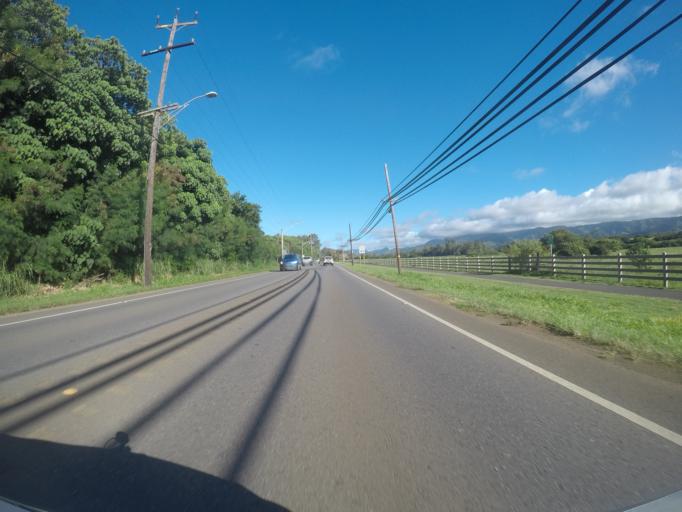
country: US
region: Hawaii
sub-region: Honolulu County
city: La'ie
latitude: 21.6610
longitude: -157.9339
